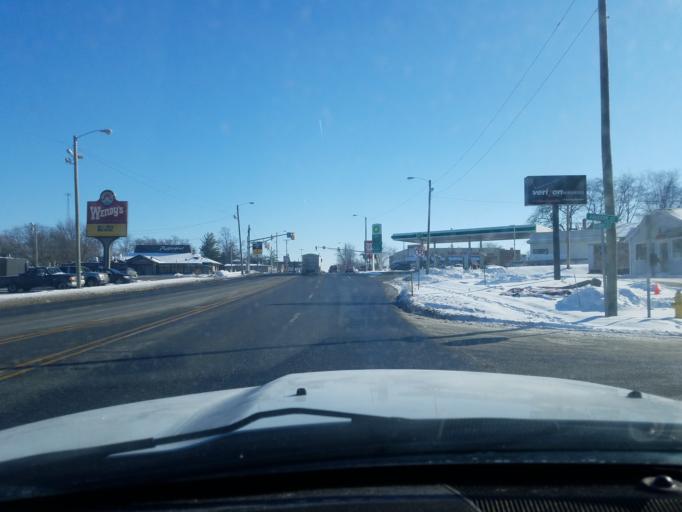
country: US
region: Indiana
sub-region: Noble County
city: Kendallville
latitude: 41.4523
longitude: -85.2688
